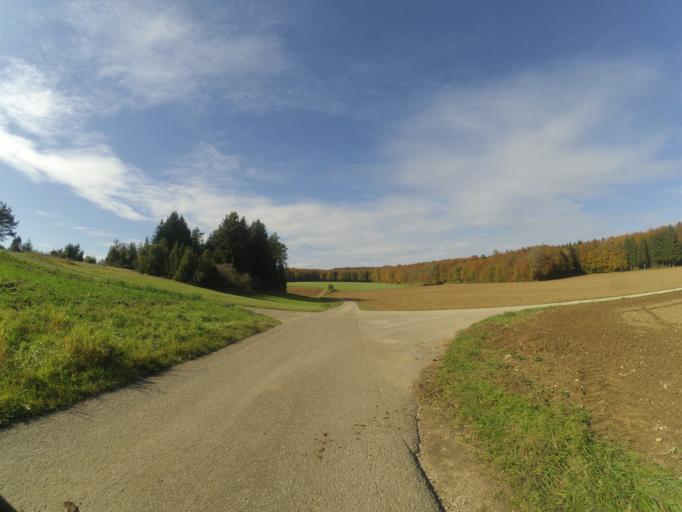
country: DE
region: Baden-Wuerttemberg
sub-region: Tuebingen Region
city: Westerstetten
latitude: 48.5422
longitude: 9.9645
